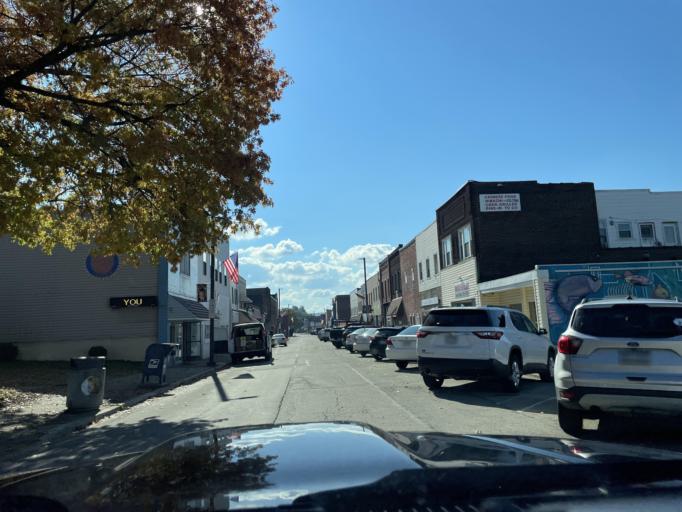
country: US
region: Pennsylvania
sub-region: Westmoreland County
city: Arnold
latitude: 40.5787
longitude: -79.7680
